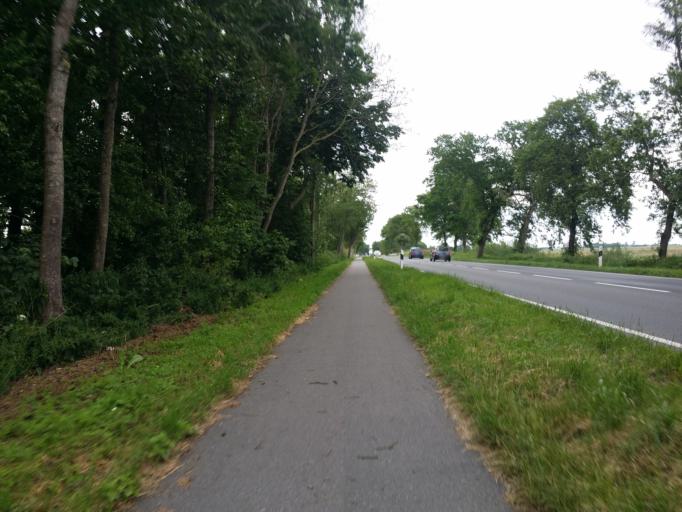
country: DE
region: Lower Saxony
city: Wittmund
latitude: 53.5895
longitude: 7.7850
